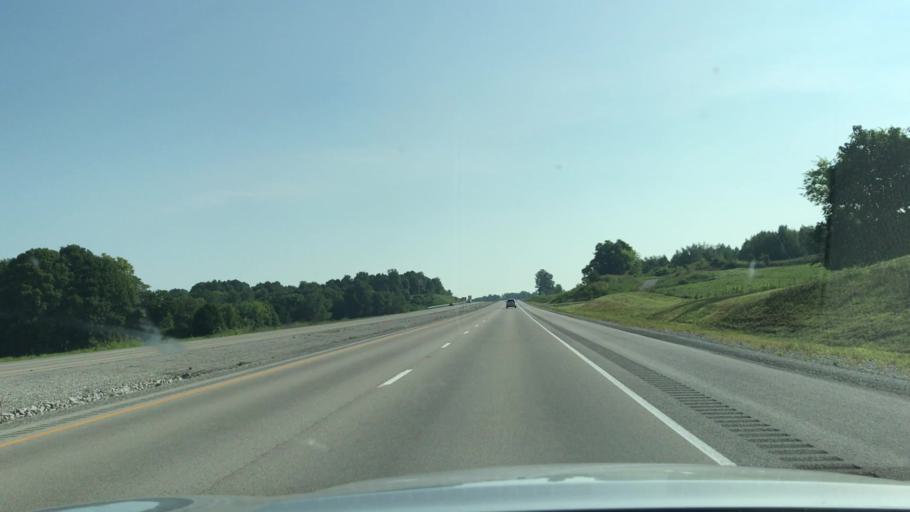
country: US
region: Kentucky
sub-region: Barren County
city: Glasgow
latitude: 37.0041
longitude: -85.9597
